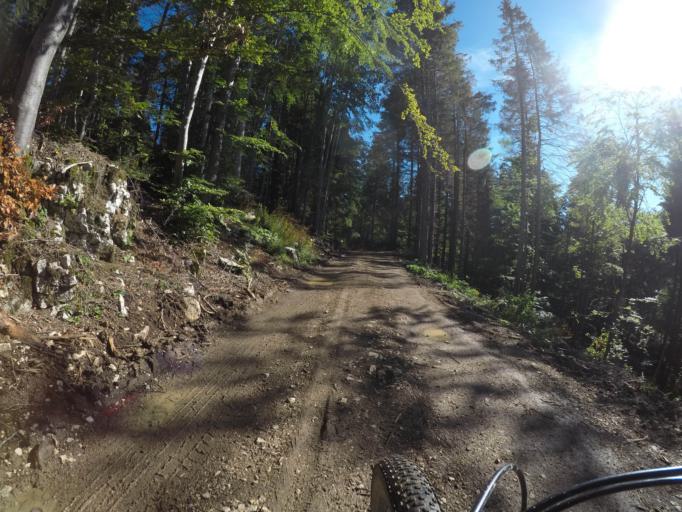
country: IT
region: Veneto
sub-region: Provincia di Vicenza
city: Canove di Roana
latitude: 45.8992
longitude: 11.4824
